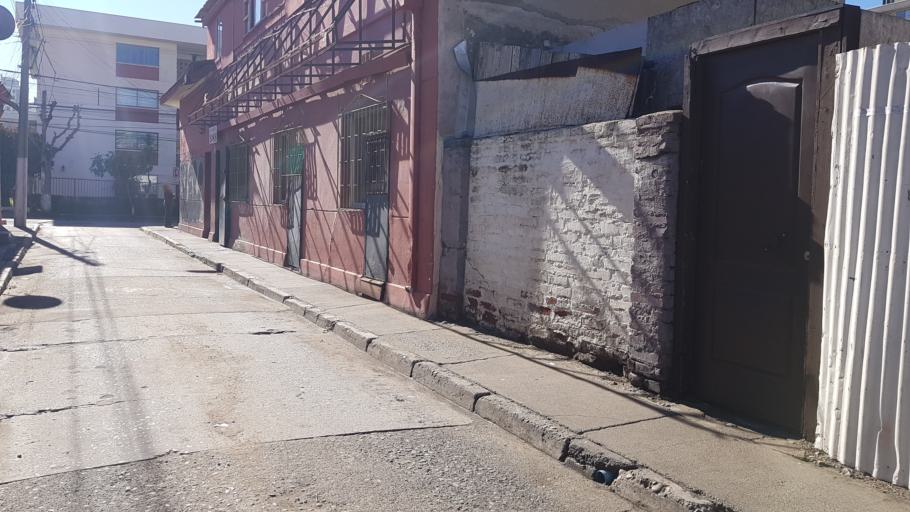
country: CL
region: Valparaiso
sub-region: Provincia de Valparaiso
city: Vina del Mar
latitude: -33.0133
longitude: -71.5518
